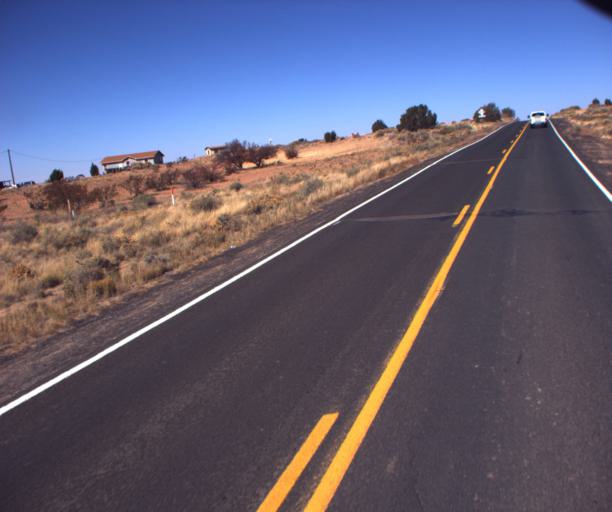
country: US
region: Arizona
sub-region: Navajo County
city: First Mesa
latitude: 35.8221
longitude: -110.5320
